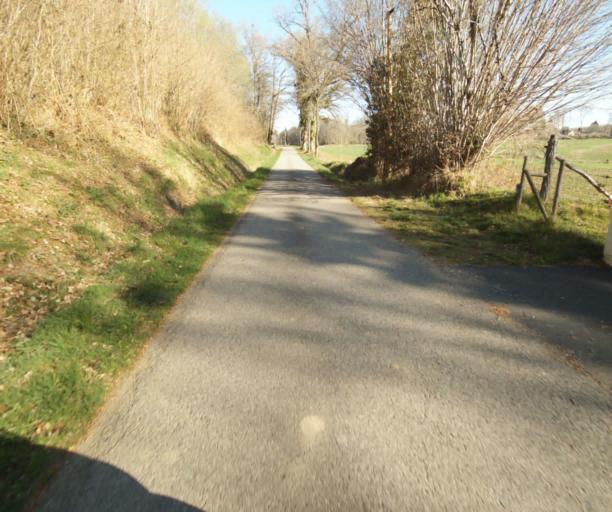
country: FR
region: Limousin
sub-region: Departement de la Correze
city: Saint-Clement
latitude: 45.3813
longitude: 1.6257
